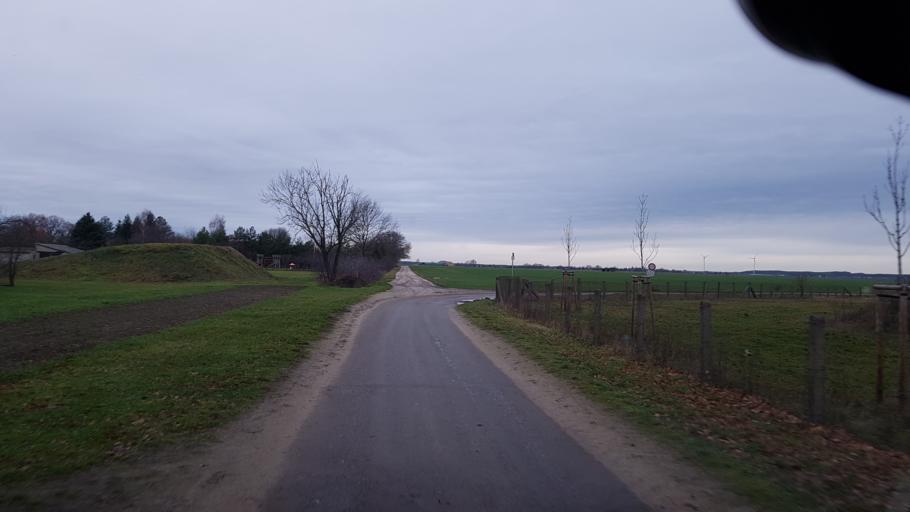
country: DE
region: Brandenburg
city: Doberlug-Kirchhain
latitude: 51.6541
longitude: 13.5398
